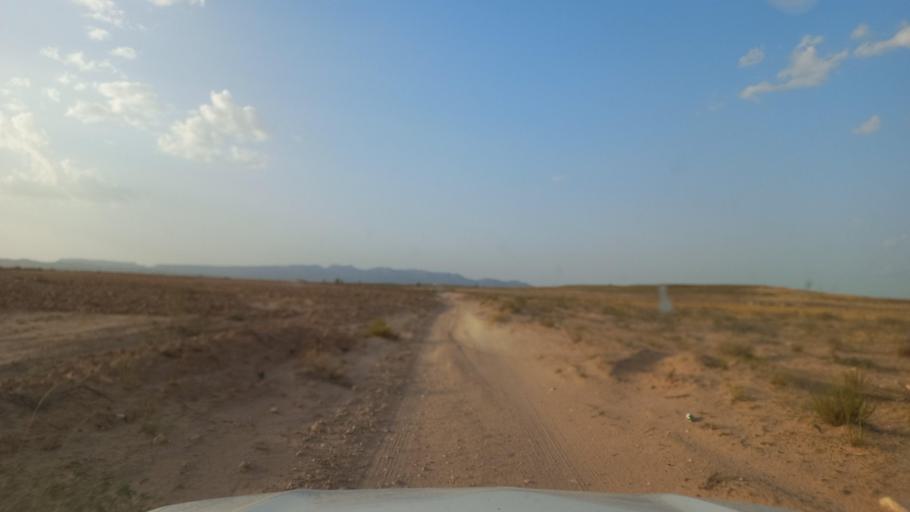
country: TN
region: Al Qasrayn
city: Sbiba
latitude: 35.3053
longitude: 9.0745
